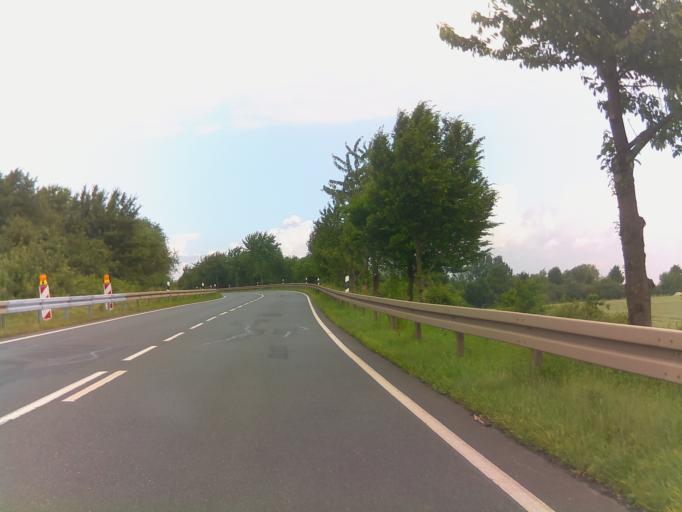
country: DE
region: Lower Saxony
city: Heyersum
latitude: 52.1825
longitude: 9.8340
